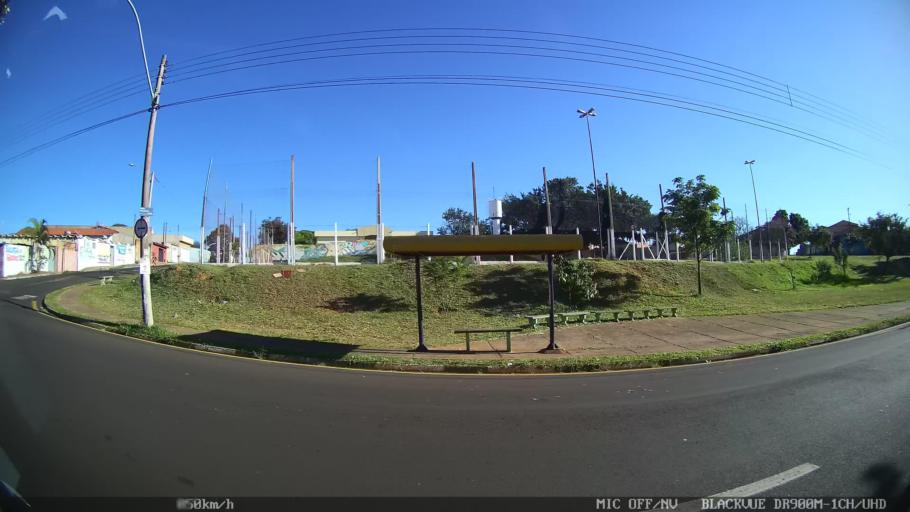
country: BR
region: Sao Paulo
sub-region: Franca
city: Franca
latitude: -20.5751
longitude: -47.3752
